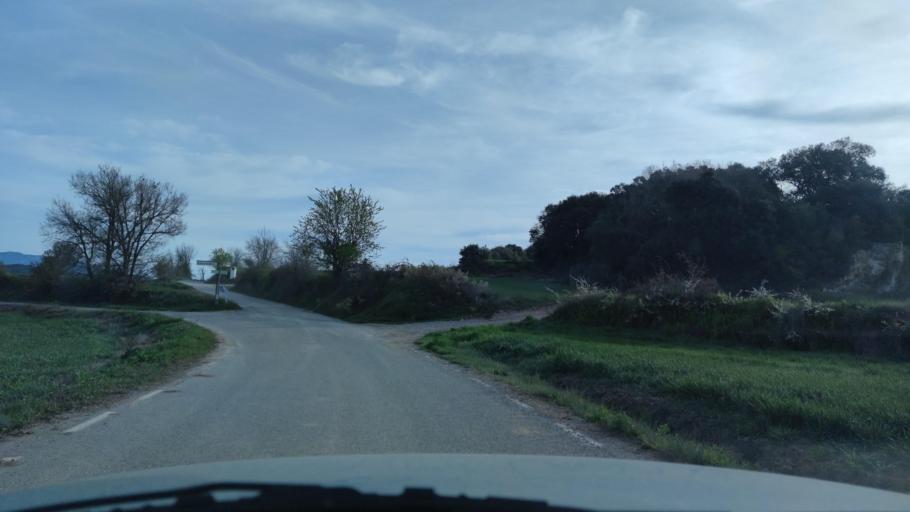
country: ES
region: Catalonia
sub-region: Provincia de Lleida
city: Os de Balaguer
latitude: 41.8805
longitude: 0.7893
